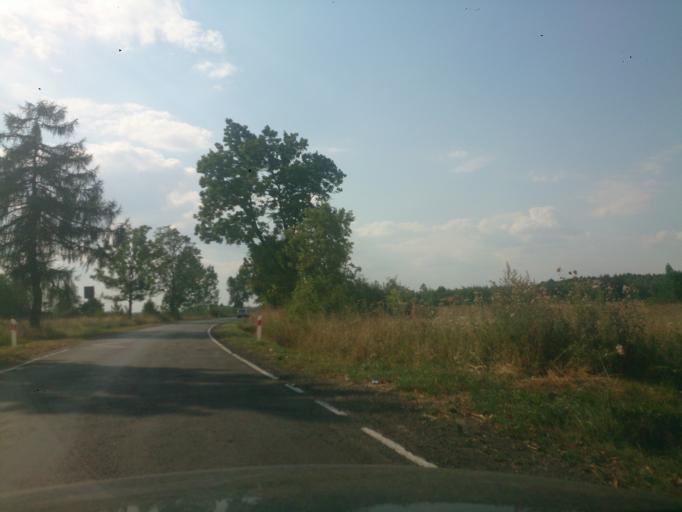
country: PL
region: Swietokrzyskie
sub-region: Powiat opatowski
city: Iwaniska
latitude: 50.6934
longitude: 21.3454
